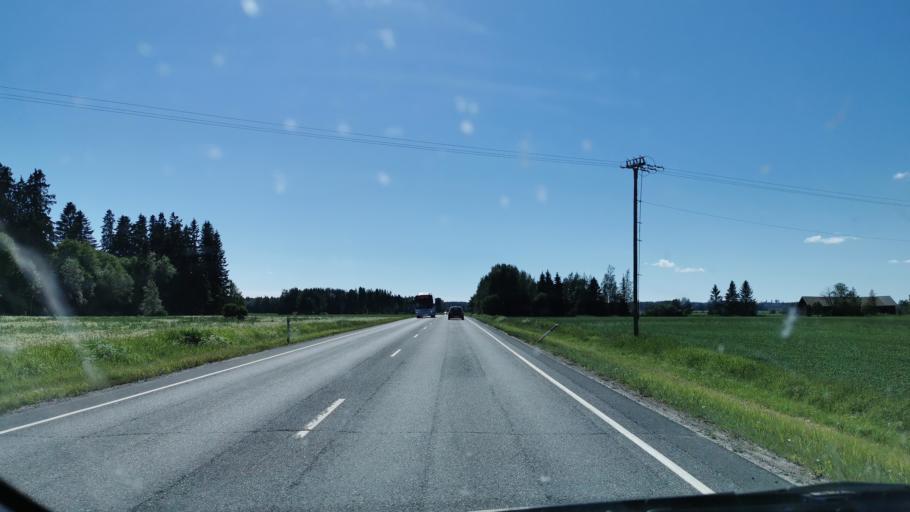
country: FI
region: Haeme
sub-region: Forssa
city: Humppila
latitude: 60.9514
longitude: 23.3299
